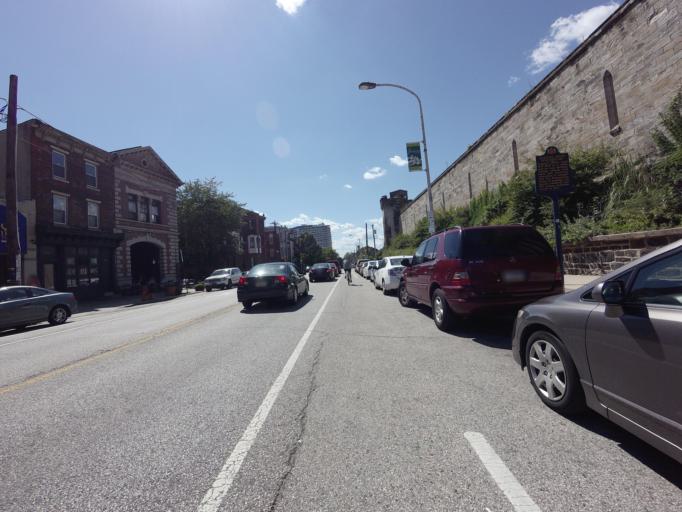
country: US
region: Pennsylvania
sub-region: Philadelphia County
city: Philadelphia
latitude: 39.9674
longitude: -75.1730
